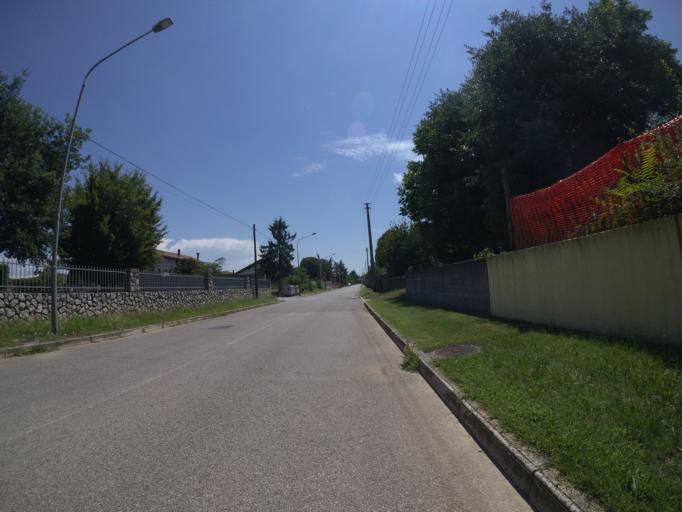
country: IT
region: Friuli Venezia Giulia
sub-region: Provincia di Udine
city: Talmassons
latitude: 45.9342
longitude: 13.1162
